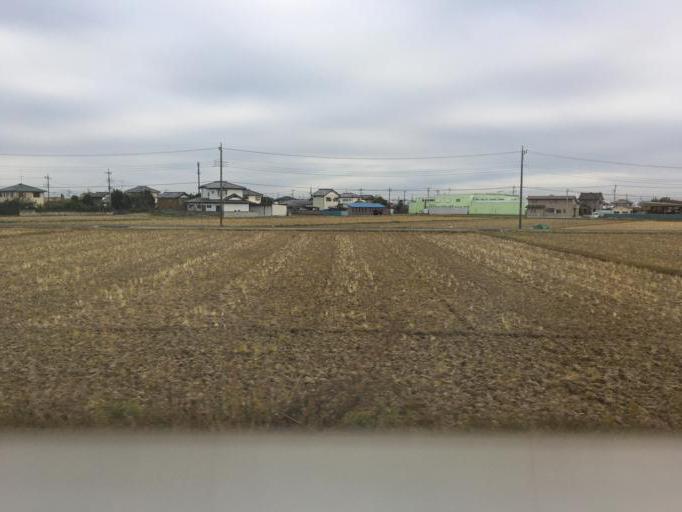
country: JP
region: Tochigi
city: Tochigi
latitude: 36.3646
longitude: 139.7177
